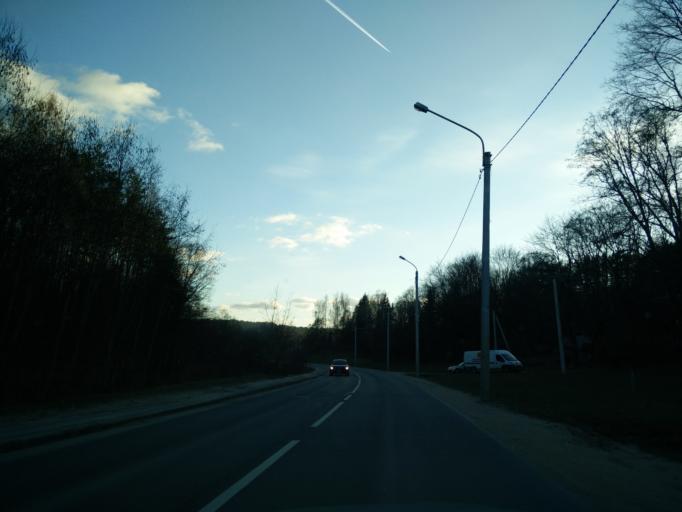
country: LT
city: Skaidiskes
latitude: 54.6989
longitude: 25.4009
